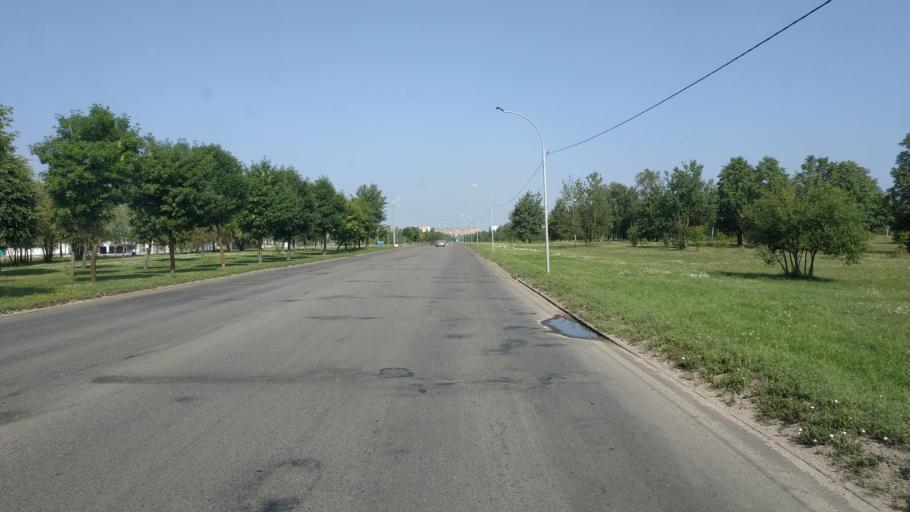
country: BY
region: Mogilev
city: Buynichy
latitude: 53.8589
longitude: 30.3268
